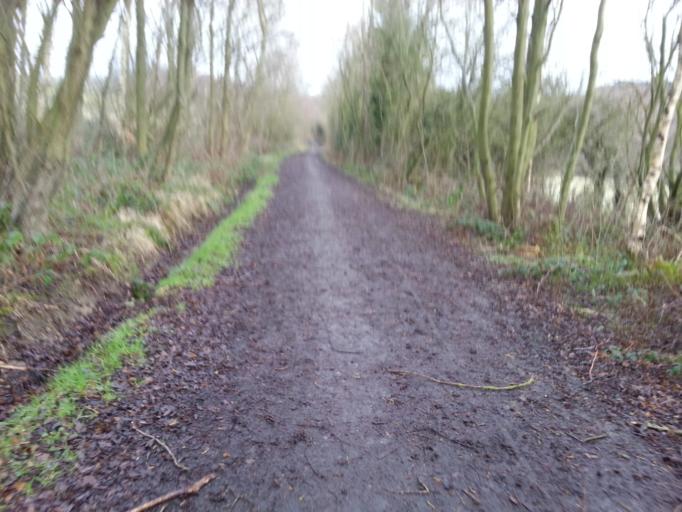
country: GB
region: England
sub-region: County Durham
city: Crook
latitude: 54.7514
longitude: -1.7332
